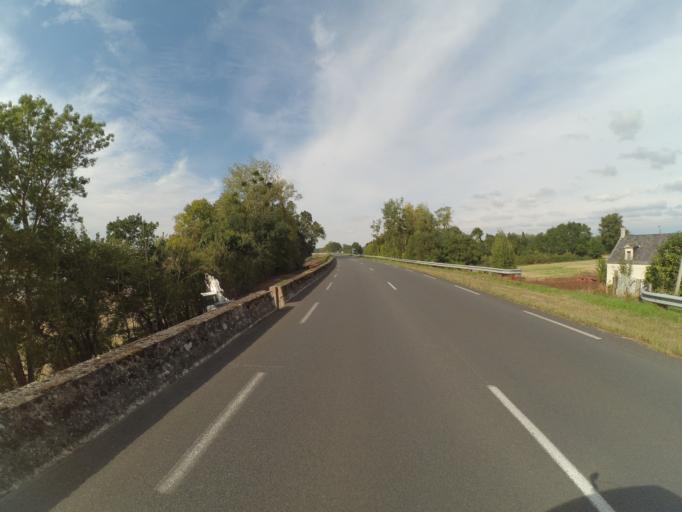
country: FR
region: Pays de la Loire
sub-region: Departement de Maine-et-Loire
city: Villebernier
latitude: 47.2434
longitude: 0.0058
